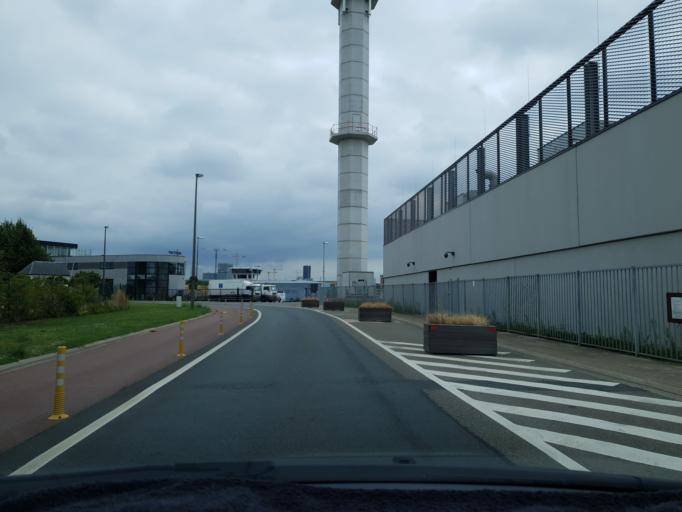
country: BE
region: Flanders
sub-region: Provincie Antwerpen
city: Antwerpen
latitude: 51.2437
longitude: 4.4086
